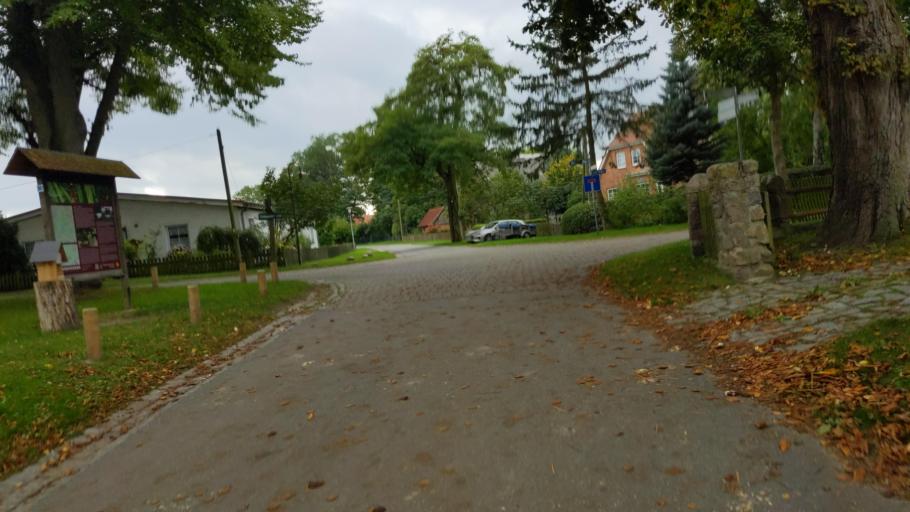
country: DE
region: Schleswig-Holstein
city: Buchholz
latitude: 53.7568
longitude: 10.7628
